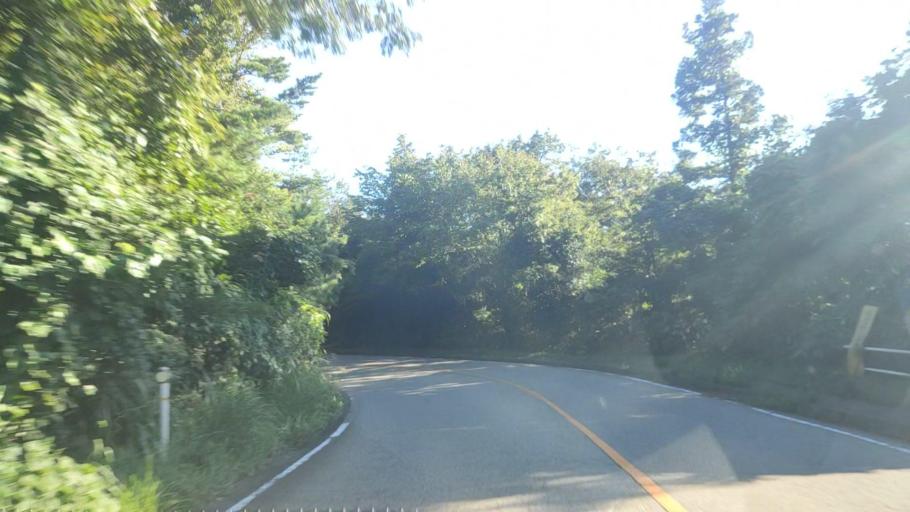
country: JP
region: Ishikawa
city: Nanao
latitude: 37.0997
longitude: 136.9499
